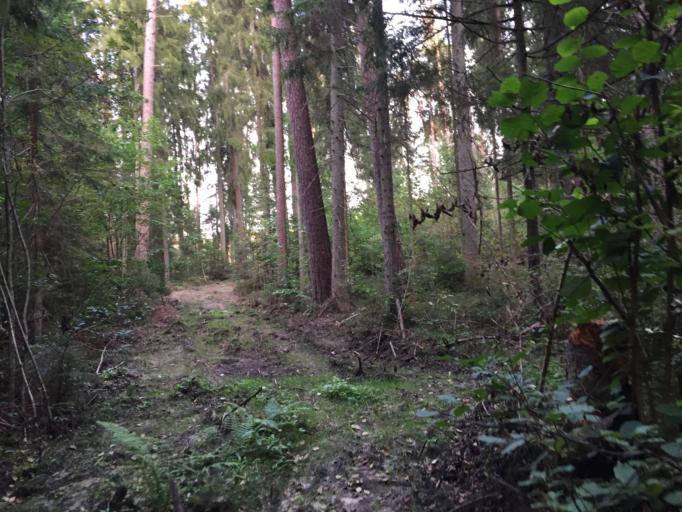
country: LV
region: Baldone
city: Baldone
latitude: 56.7551
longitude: 24.4054
